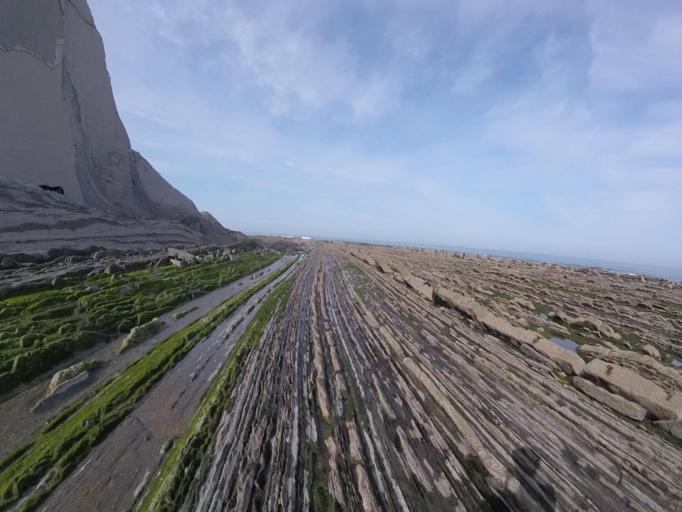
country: ES
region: Basque Country
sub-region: Provincia de Guipuzcoa
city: Deba
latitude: 43.2981
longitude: -2.3097
